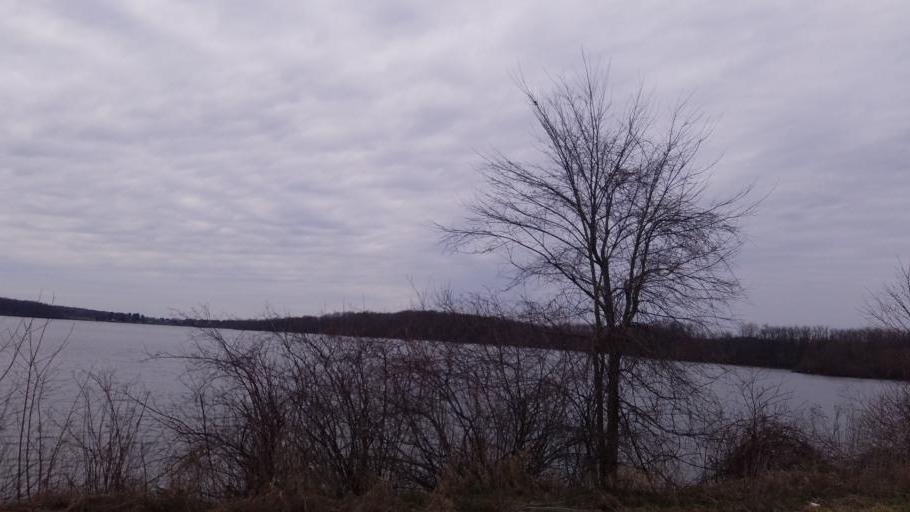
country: US
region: Ohio
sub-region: Knox County
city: Fredericktown
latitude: 40.5185
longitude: -82.4836
